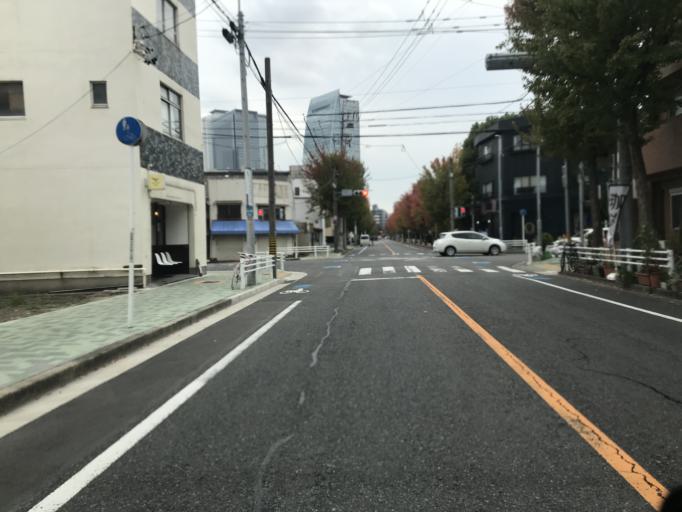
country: JP
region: Aichi
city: Nagoya-shi
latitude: 35.1812
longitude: 136.8825
